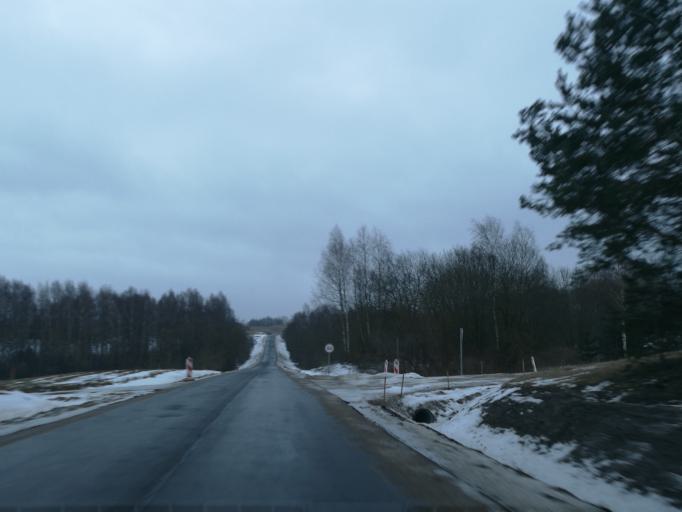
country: LT
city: Trakai
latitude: 54.6840
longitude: 24.9755
